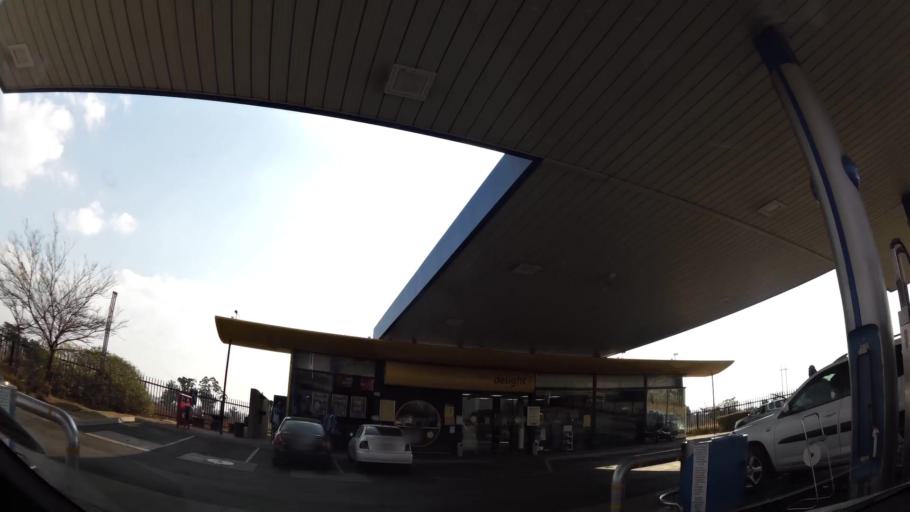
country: ZA
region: Gauteng
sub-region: Ekurhuleni Metropolitan Municipality
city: Boksburg
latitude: -26.2302
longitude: 28.2482
